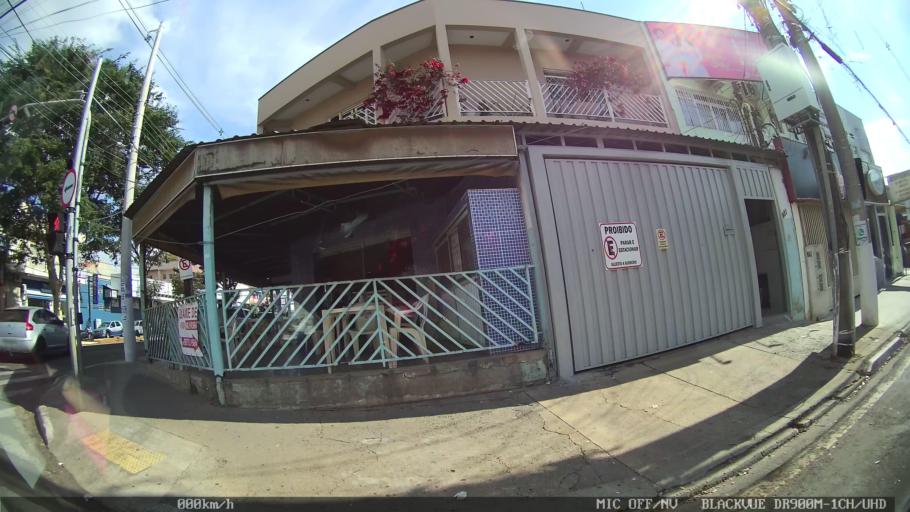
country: BR
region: Sao Paulo
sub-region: Hortolandia
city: Hortolandia
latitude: -22.9024
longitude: -47.2417
